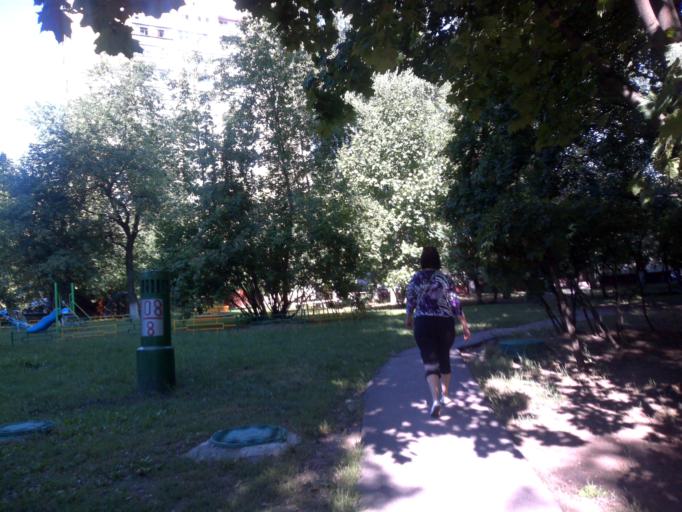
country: RU
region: Moskovskaya
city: Leninskiye Gory
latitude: 55.6940
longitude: 37.5694
